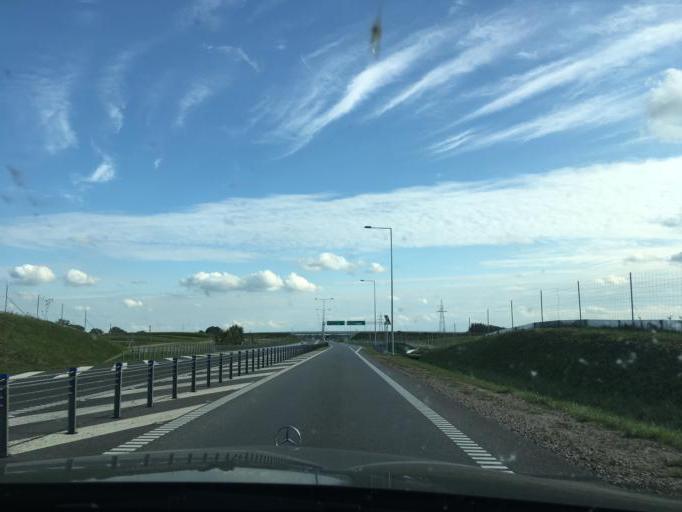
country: PL
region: Podlasie
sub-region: Powiat augustowski
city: Augustow
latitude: 53.8479
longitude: 22.9385
